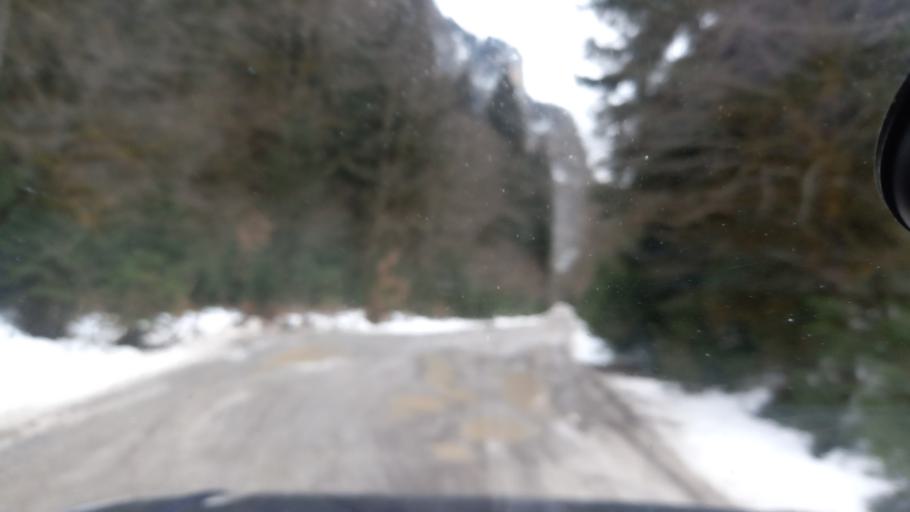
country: GE
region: Abkhazia
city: Gagra
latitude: 43.4320
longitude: 40.4460
